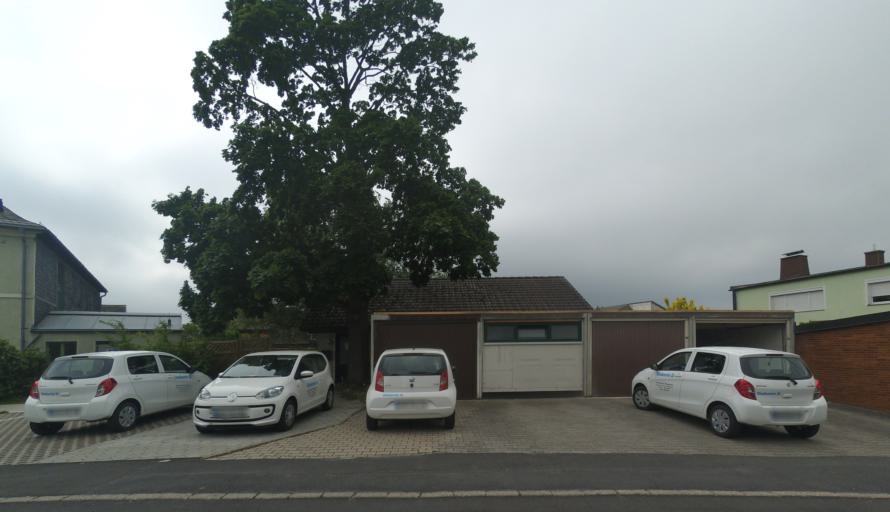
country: DE
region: Bavaria
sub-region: Upper Franconia
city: Roslau
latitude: 50.0858
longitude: 11.9683
